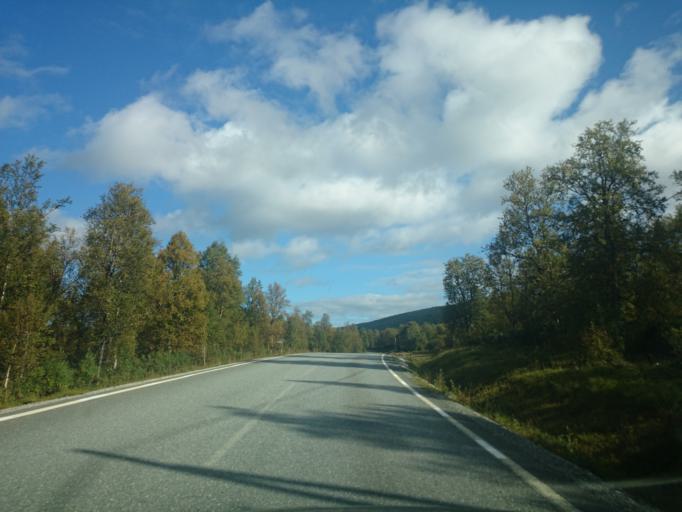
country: NO
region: Sor-Trondelag
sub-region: Tydal
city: Aas
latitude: 62.6554
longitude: 12.4265
